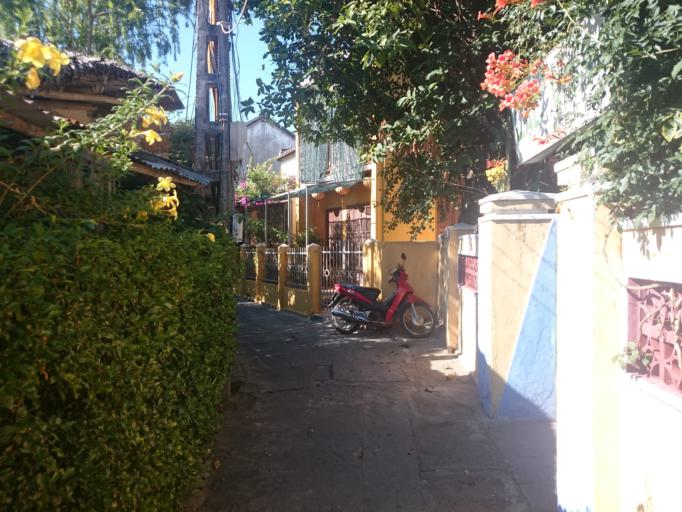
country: VN
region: Quang Nam
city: Hoi An
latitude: 15.8779
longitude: 108.3306
